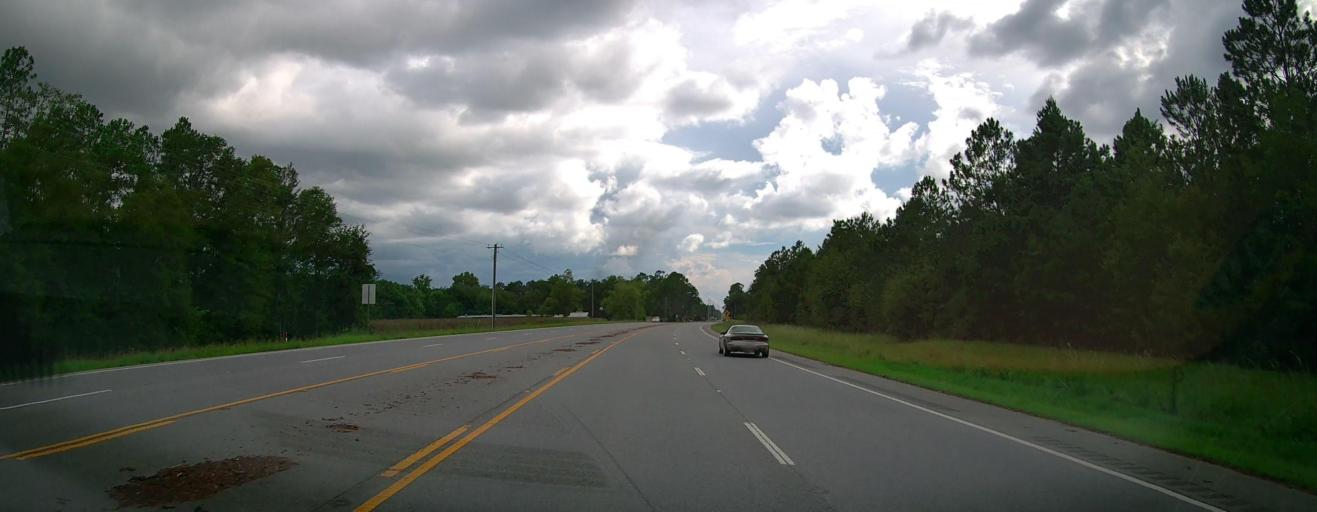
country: US
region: Georgia
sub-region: Pierce County
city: Blackshear
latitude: 31.4145
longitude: -82.1060
